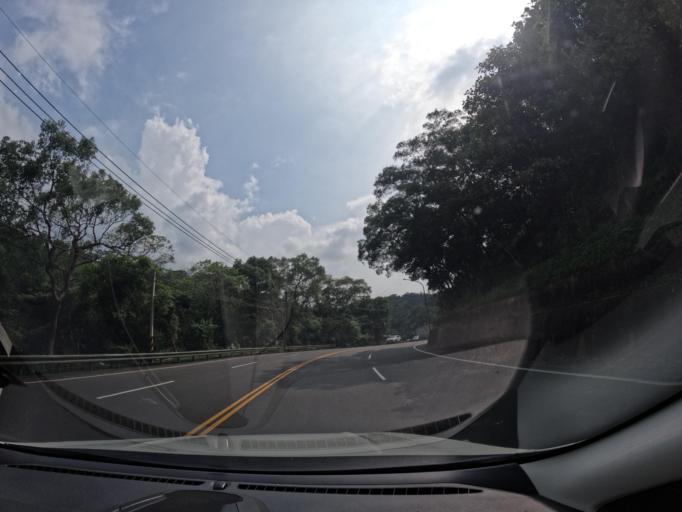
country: TW
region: Taiwan
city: Daxi
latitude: 24.9032
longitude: 121.3435
